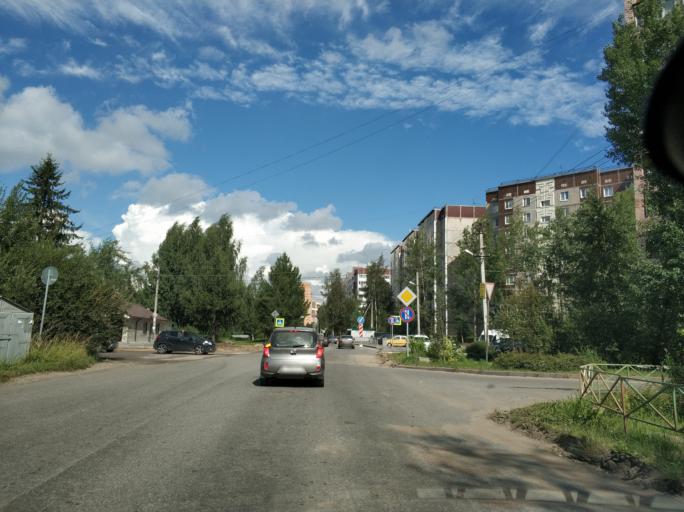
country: RU
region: Leningrad
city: Vsevolozhsk
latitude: 60.0242
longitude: 30.6225
